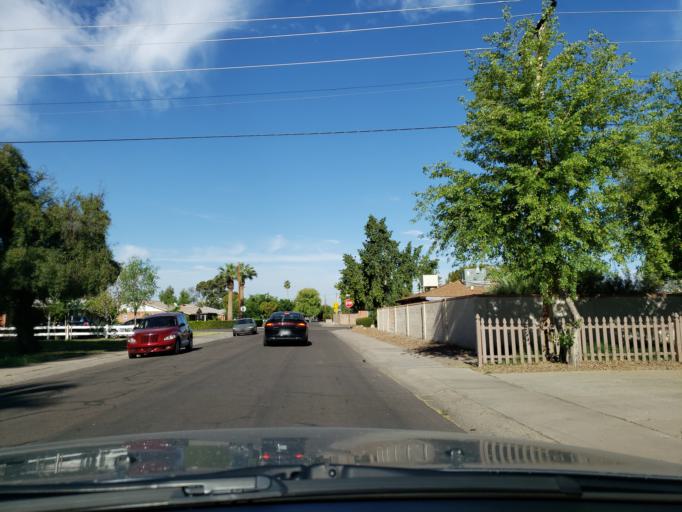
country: US
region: Arizona
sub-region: Maricopa County
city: Phoenix
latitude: 33.5176
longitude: -112.0861
